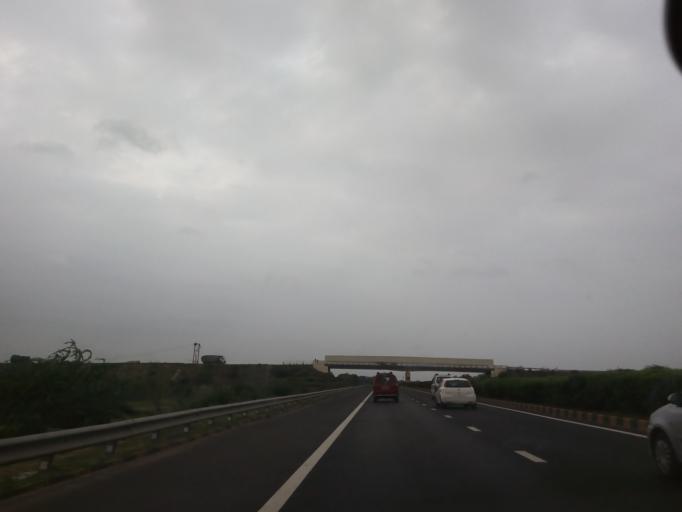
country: IN
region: Gujarat
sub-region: Kheda
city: Mahemdavad
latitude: 22.8242
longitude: 72.8287
